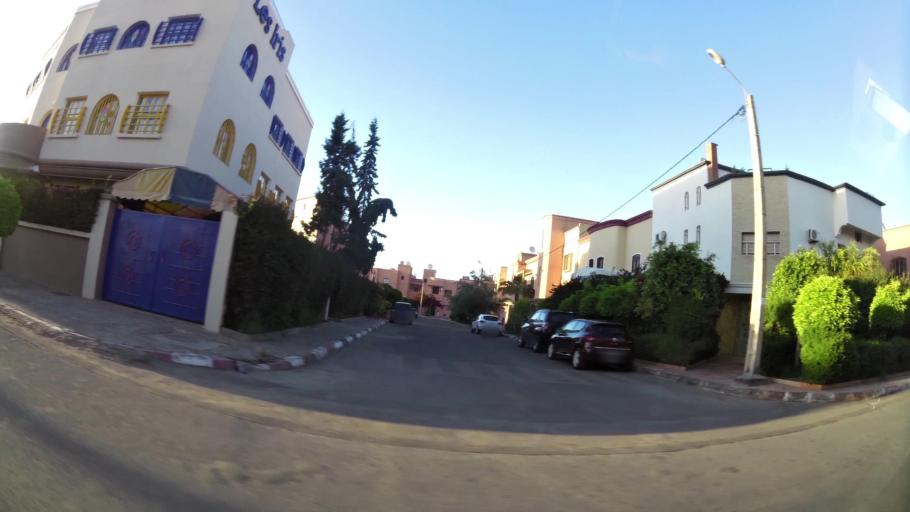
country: MA
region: Marrakech-Tensift-Al Haouz
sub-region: Marrakech
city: Marrakesh
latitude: 31.6544
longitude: -8.0341
